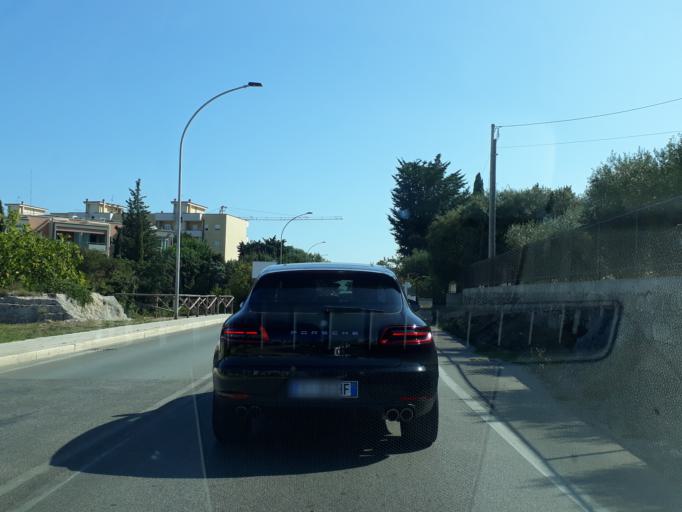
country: IT
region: Apulia
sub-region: Provincia di Bari
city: Monopoli
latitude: 40.9461
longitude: 17.2943
